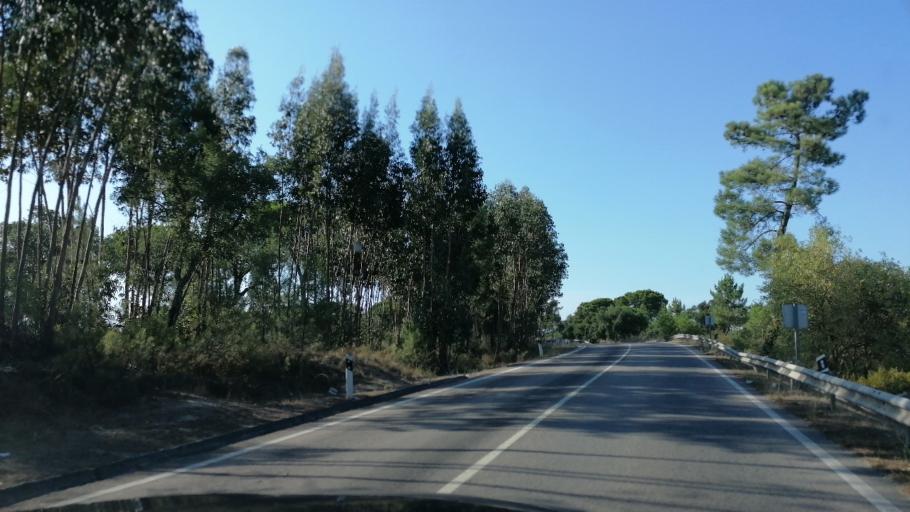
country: PT
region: Santarem
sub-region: Coruche
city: Coruche
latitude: 38.9729
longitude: -8.5386
